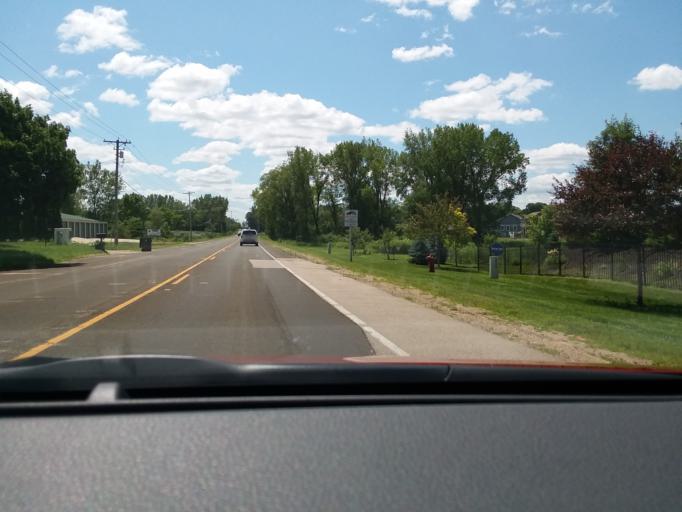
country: US
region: Wisconsin
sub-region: Dane County
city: Windsor
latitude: 43.2156
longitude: -89.3433
